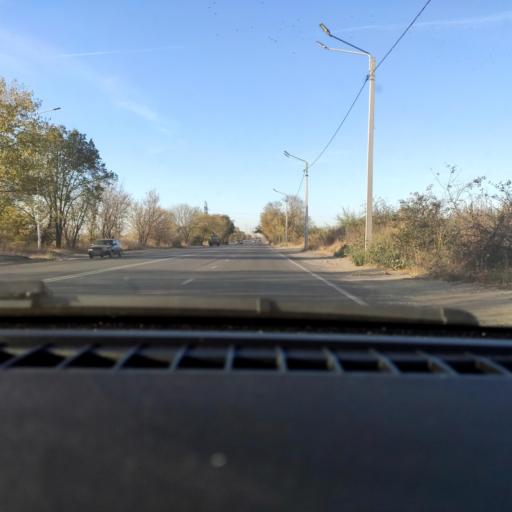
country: RU
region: Voronezj
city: Maslovka
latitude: 51.6267
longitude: 39.2840
